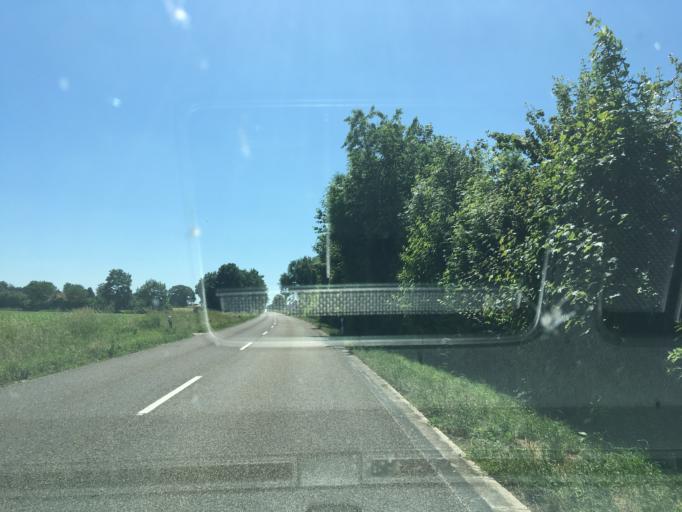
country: DE
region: North Rhine-Westphalia
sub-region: Regierungsbezirk Munster
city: Raesfeld
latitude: 51.7899
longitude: 6.8142
